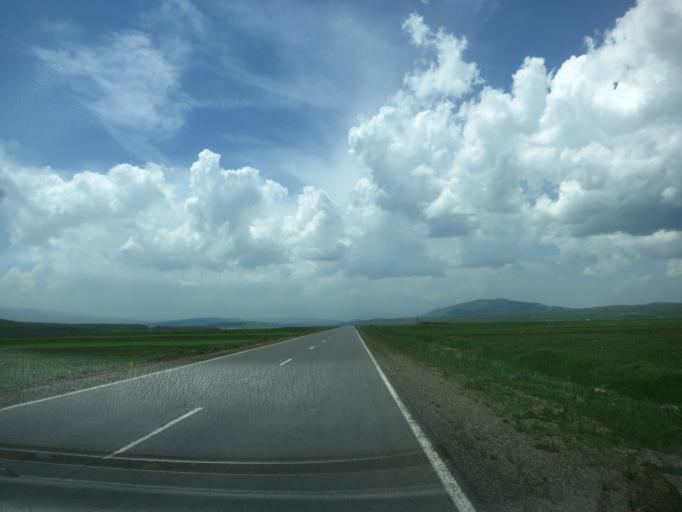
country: GE
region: Samtskhe-Javakheti
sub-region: Ninotsminda
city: Ninotsminda
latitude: 41.2937
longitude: 43.6898
